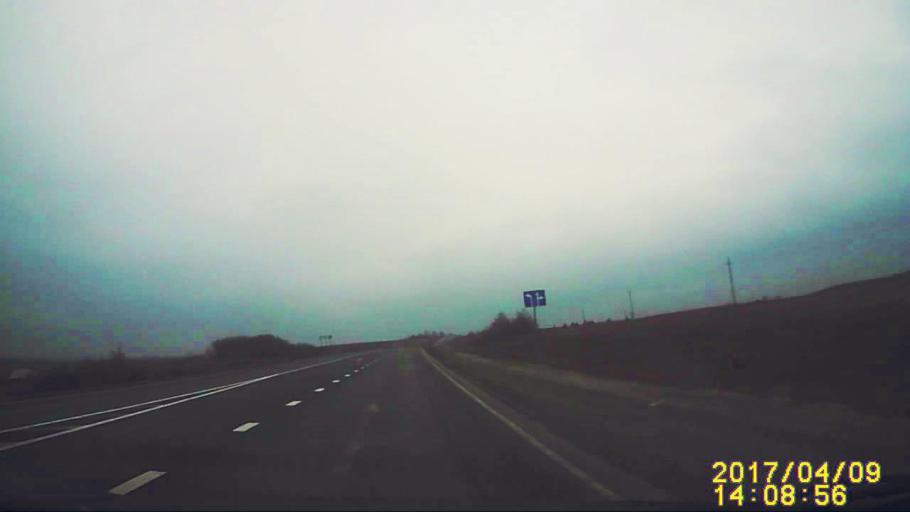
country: RU
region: Ulyanovsk
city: Silikatnyy
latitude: 54.0243
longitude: 48.2142
